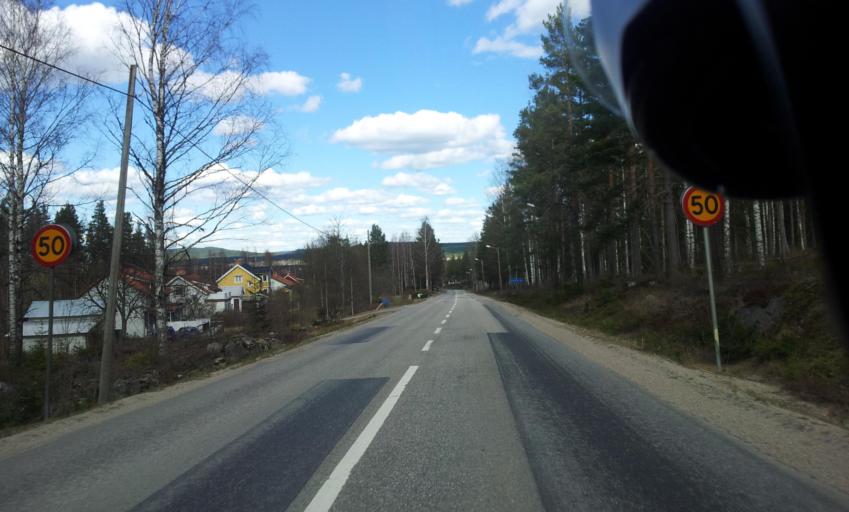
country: SE
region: Gaevleborg
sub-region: Ovanakers Kommun
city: Edsbyn
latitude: 61.3589
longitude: 15.8103
